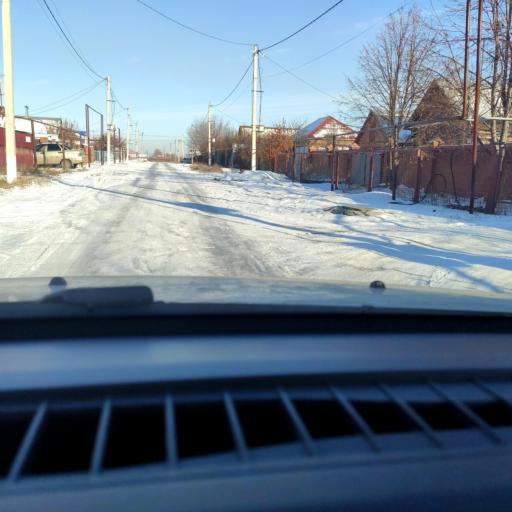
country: RU
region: Samara
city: Podstepki
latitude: 53.5174
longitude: 49.1281
